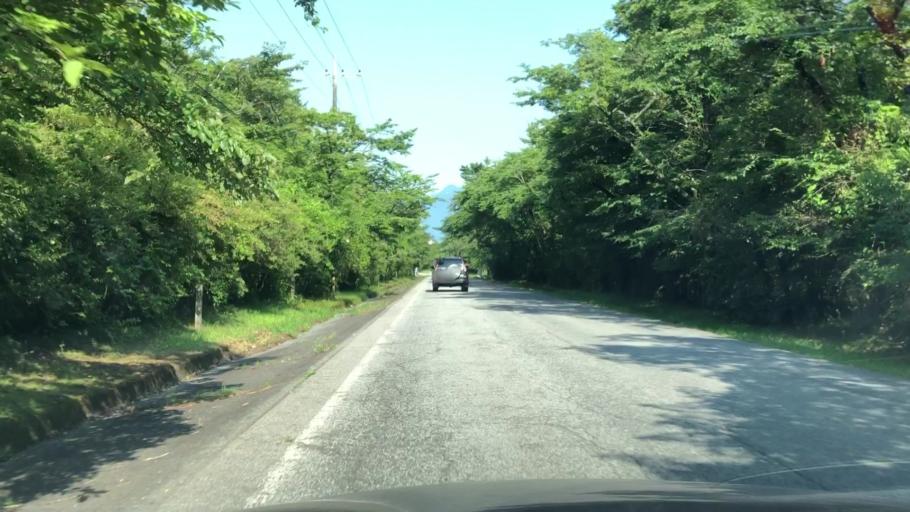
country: JP
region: Shizuoka
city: Gotemba
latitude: 35.3262
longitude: 138.8580
